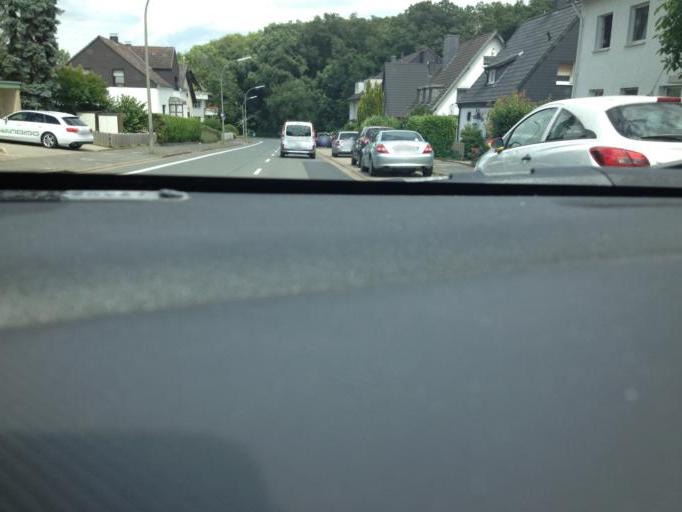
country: DE
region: North Rhine-Westphalia
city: Herdecke
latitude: 51.4508
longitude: 7.4626
